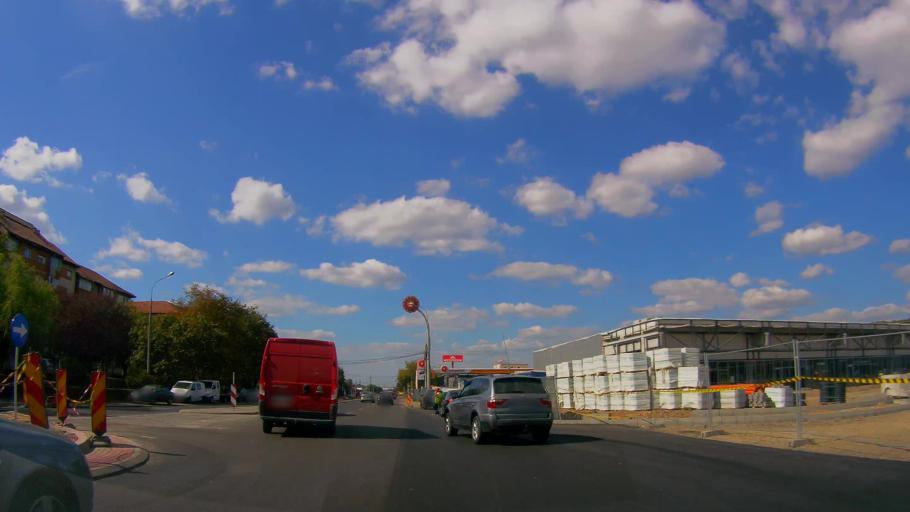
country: RO
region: Salaj
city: Zalau
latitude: 47.2007
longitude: 23.0554
